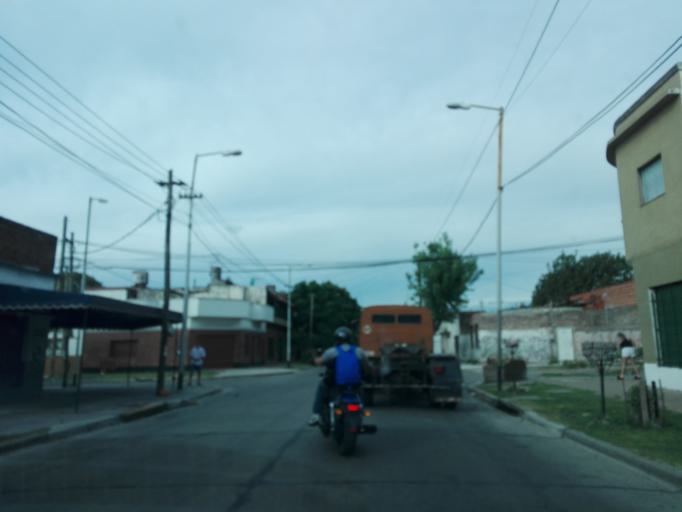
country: AR
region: Buenos Aires
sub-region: Partido de Avellaneda
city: Avellaneda
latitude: -34.6926
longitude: -58.3558
